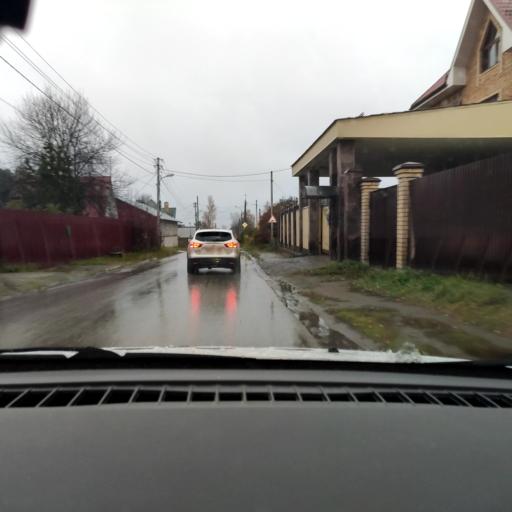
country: RU
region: Perm
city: Kondratovo
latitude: 58.0461
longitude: 56.1198
